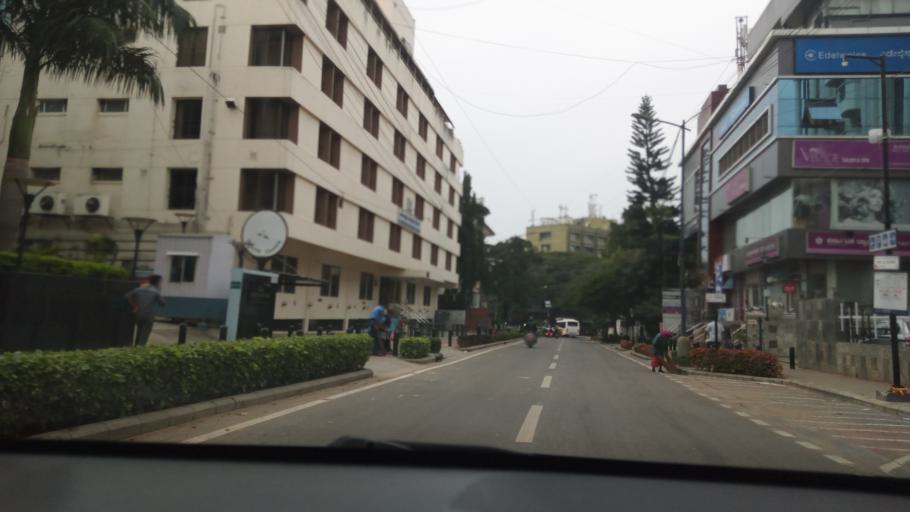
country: IN
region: Karnataka
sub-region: Bangalore Urban
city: Bangalore
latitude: 12.9693
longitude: 77.6005
